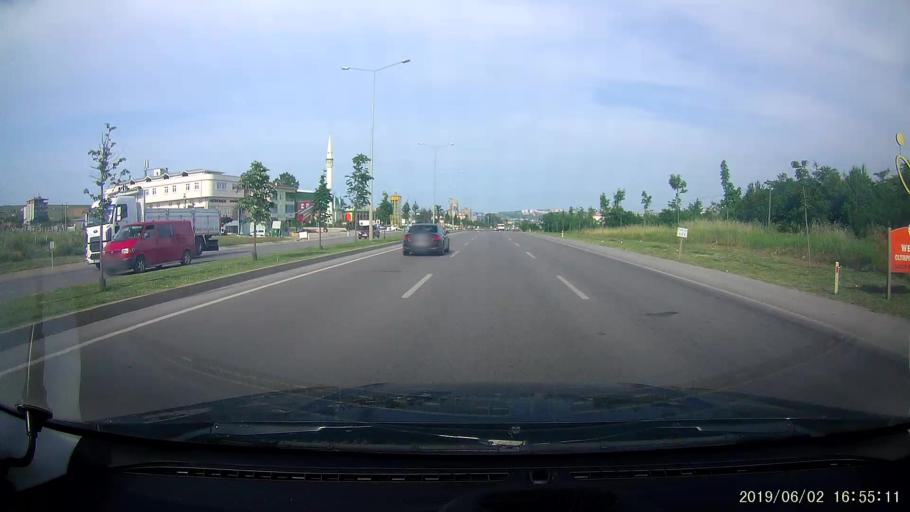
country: TR
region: Samsun
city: Samsun
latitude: 41.2927
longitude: 36.2484
